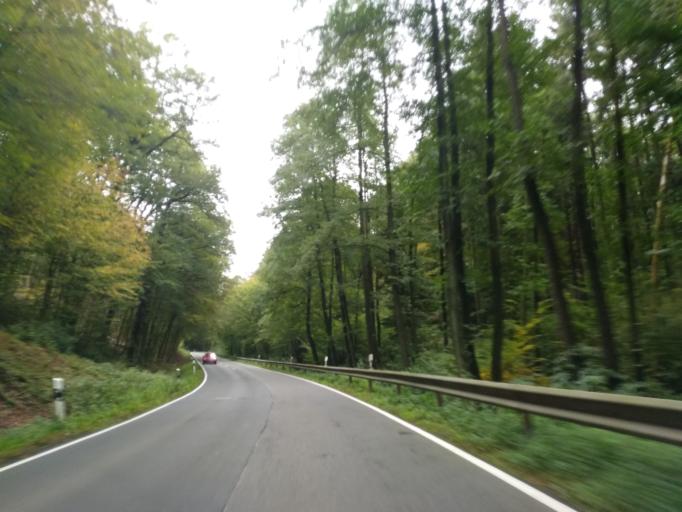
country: DE
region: North Rhine-Westphalia
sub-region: Regierungsbezirk Koln
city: Bad Honnef
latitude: 50.6661
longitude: 7.2897
